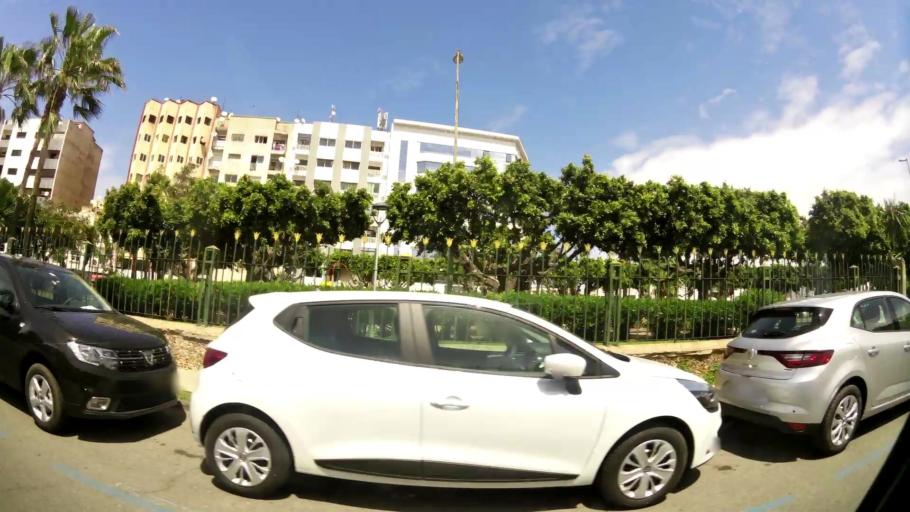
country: MA
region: Grand Casablanca
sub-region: Casablanca
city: Casablanca
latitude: 33.5990
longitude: -7.6329
